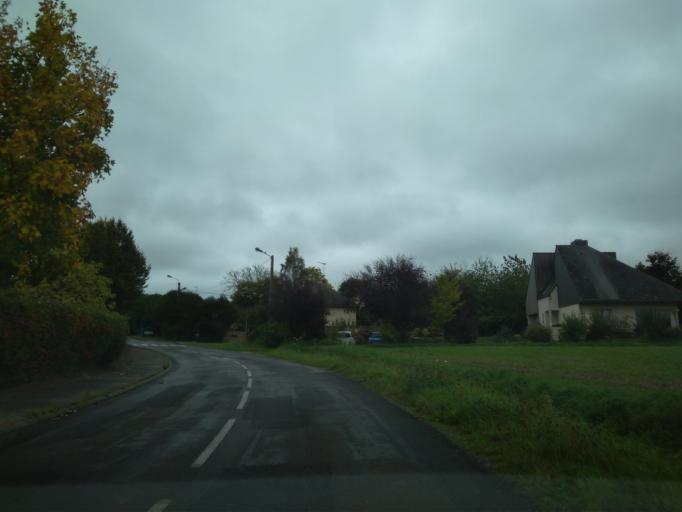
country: FR
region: Brittany
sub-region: Departement d'Ille-et-Vilaine
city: Betton
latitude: 48.1720
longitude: -1.6351
